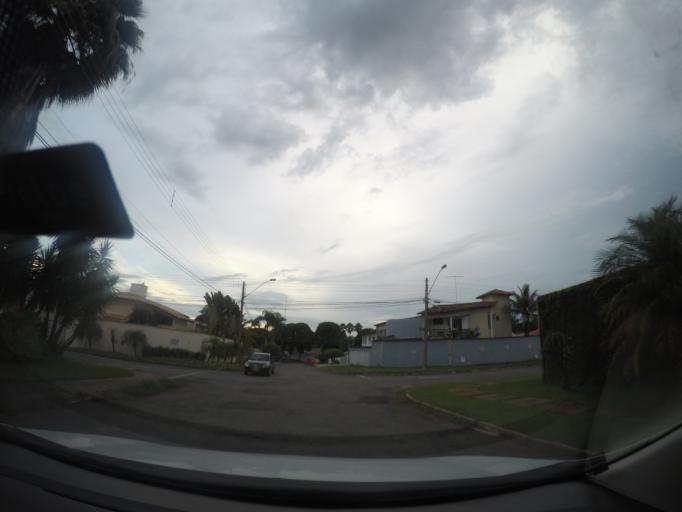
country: BR
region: Goias
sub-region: Goiania
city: Goiania
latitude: -16.6538
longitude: -49.2280
